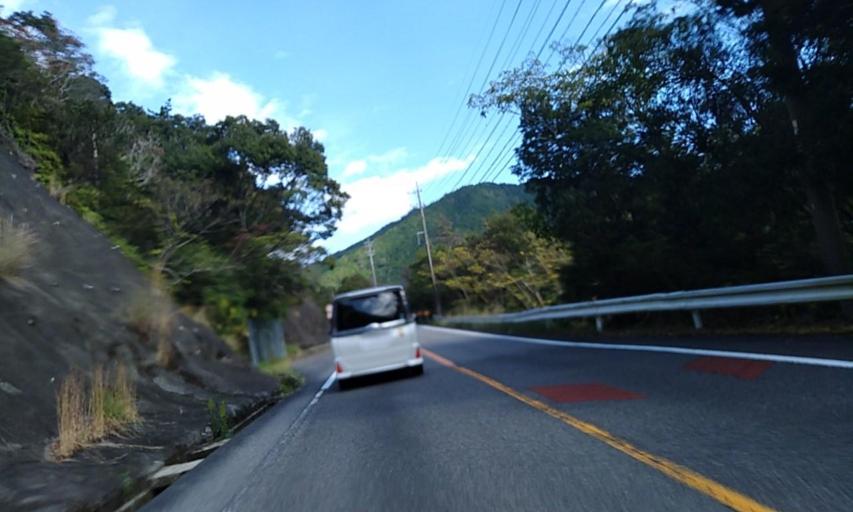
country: JP
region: Mie
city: Owase
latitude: 34.2115
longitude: 136.3628
